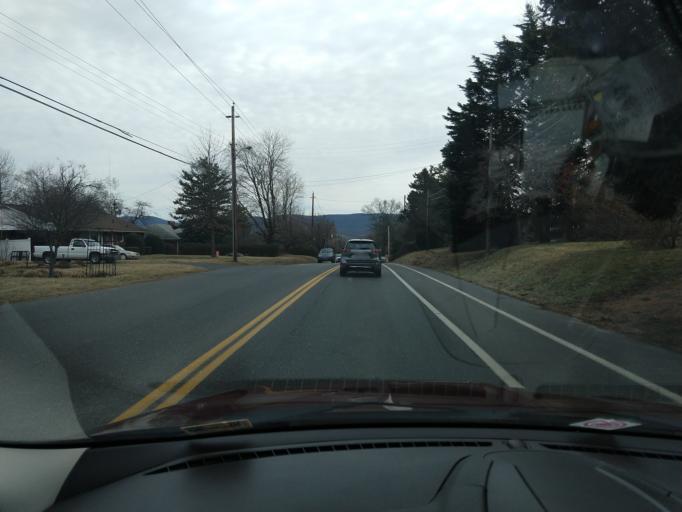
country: US
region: Virginia
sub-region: City of Waynesboro
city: Waynesboro
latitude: 38.0758
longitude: -78.9115
